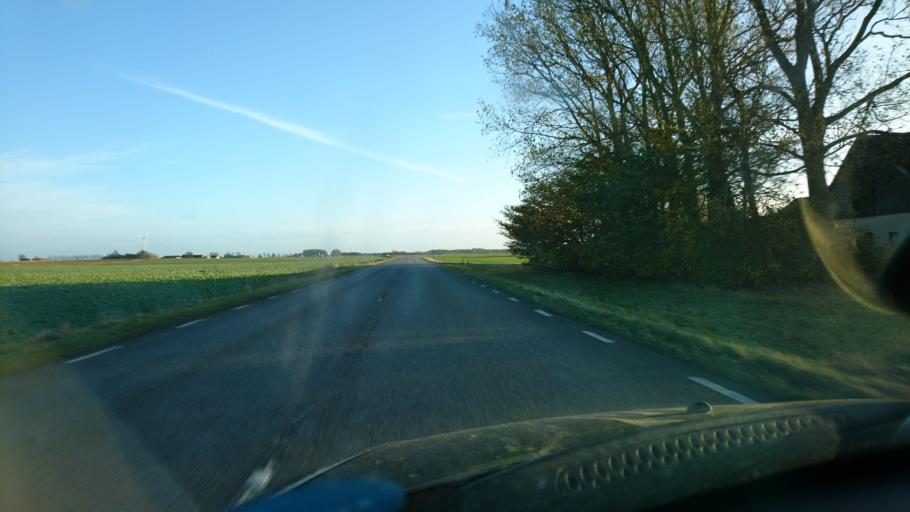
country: SE
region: Skane
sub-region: Simrishamns Kommun
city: Simrishamn
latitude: 55.4849
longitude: 14.1689
